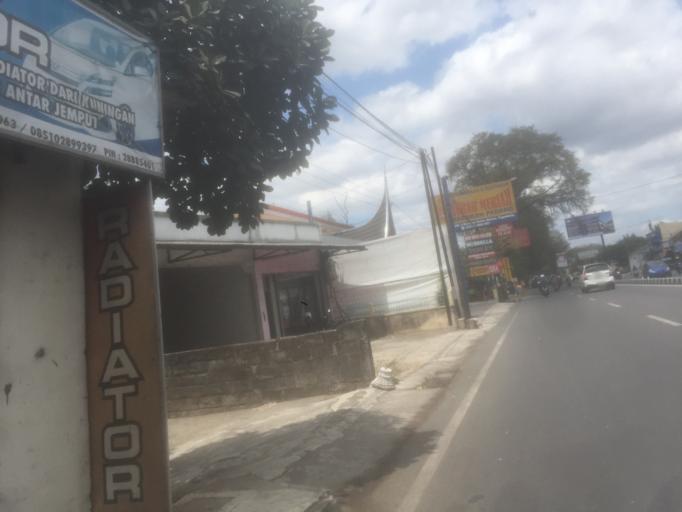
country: ID
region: Daerah Istimewa Yogyakarta
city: Melati
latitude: -7.7255
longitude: 110.3625
